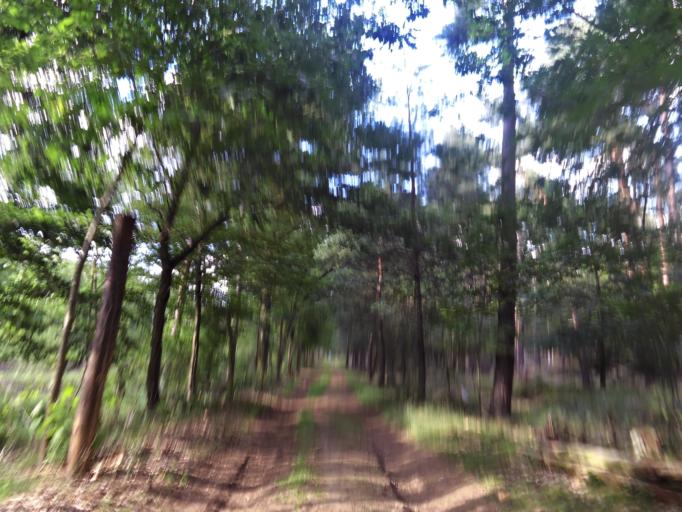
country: DE
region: Hesse
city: Niederrad
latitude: 50.0488
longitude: 8.6141
